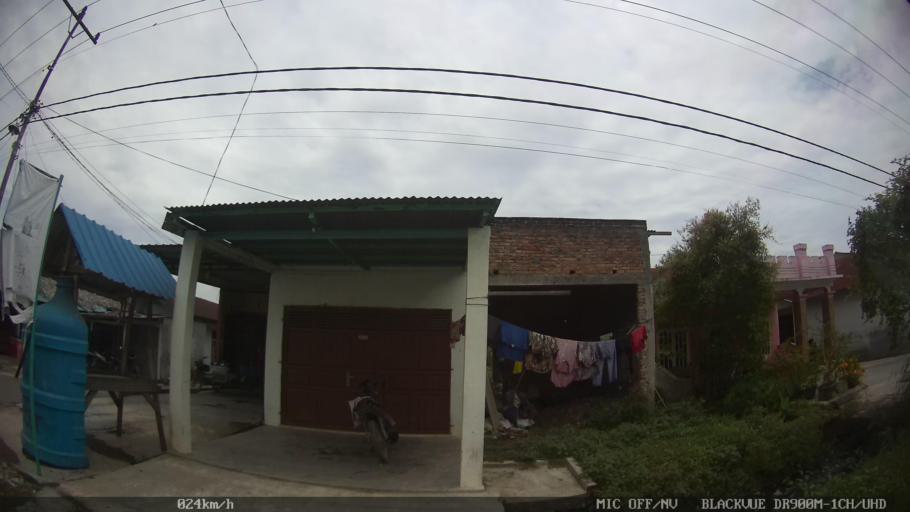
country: ID
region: North Sumatra
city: Sunggal
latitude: 3.6327
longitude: 98.5667
